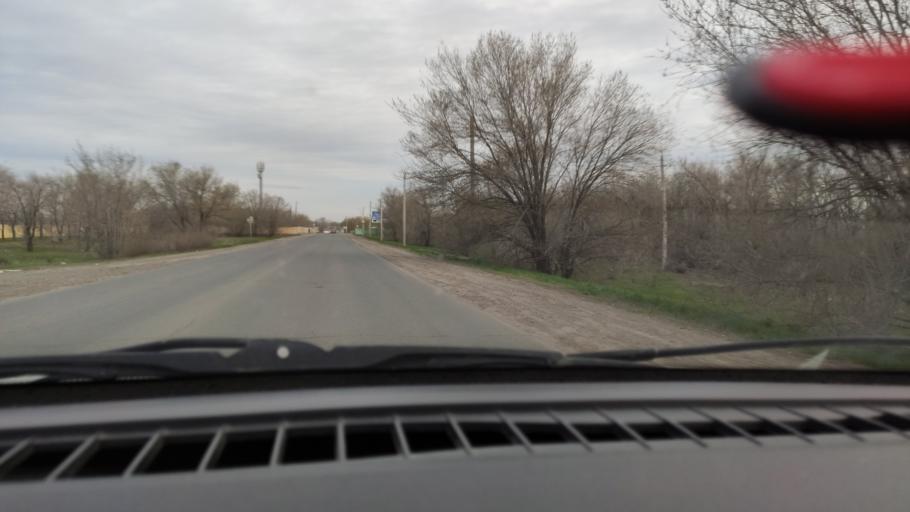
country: RU
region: Orenburg
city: Tatarskaya Kargala
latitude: 51.8844
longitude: 55.1537
